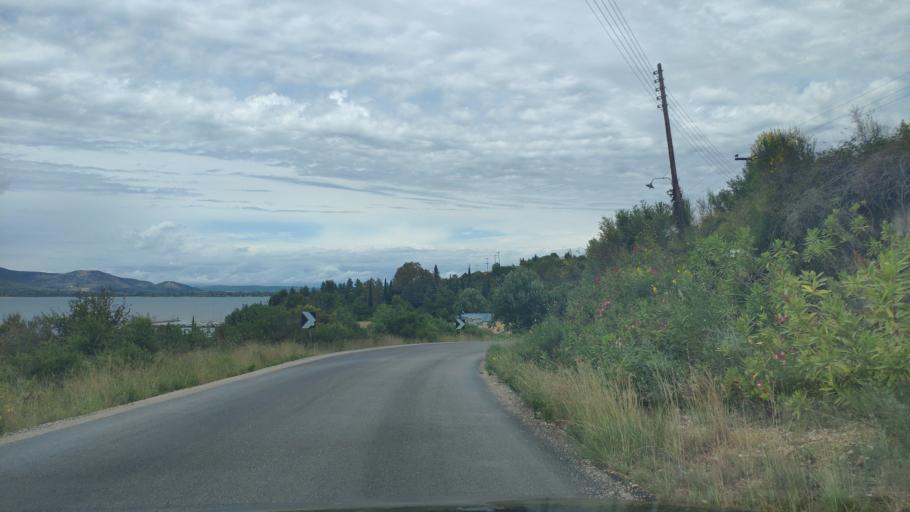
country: GR
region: West Greece
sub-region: Nomos Aitolias kai Akarnanias
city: Palairos
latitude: 38.7647
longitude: 20.8815
